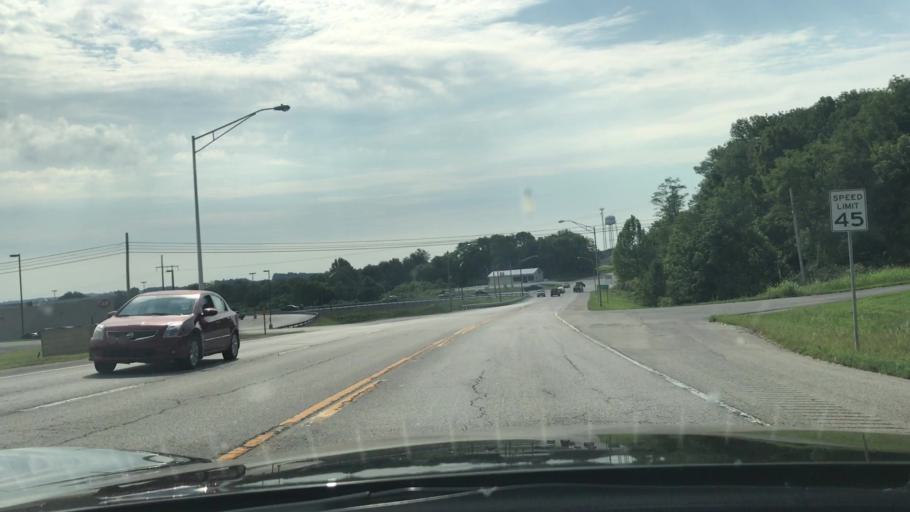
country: US
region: Kentucky
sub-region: Green County
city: Greensburg
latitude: 37.2721
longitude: -85.4988
